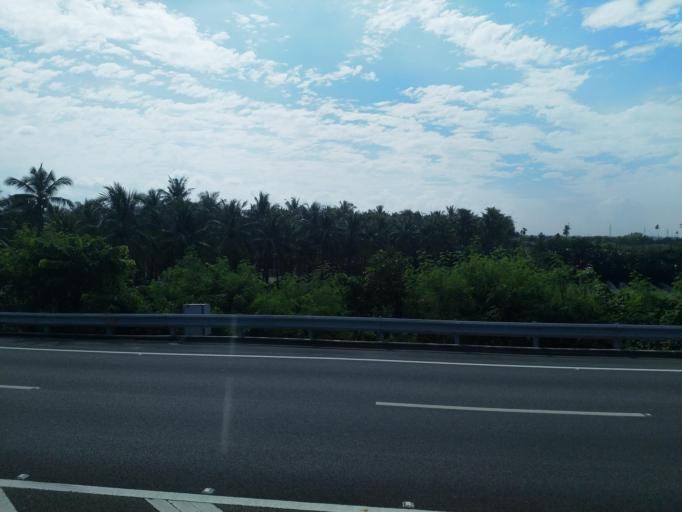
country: TW
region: Taiwan
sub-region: Pingtung
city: Pingtung
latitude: 22.7997
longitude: 120.4740
